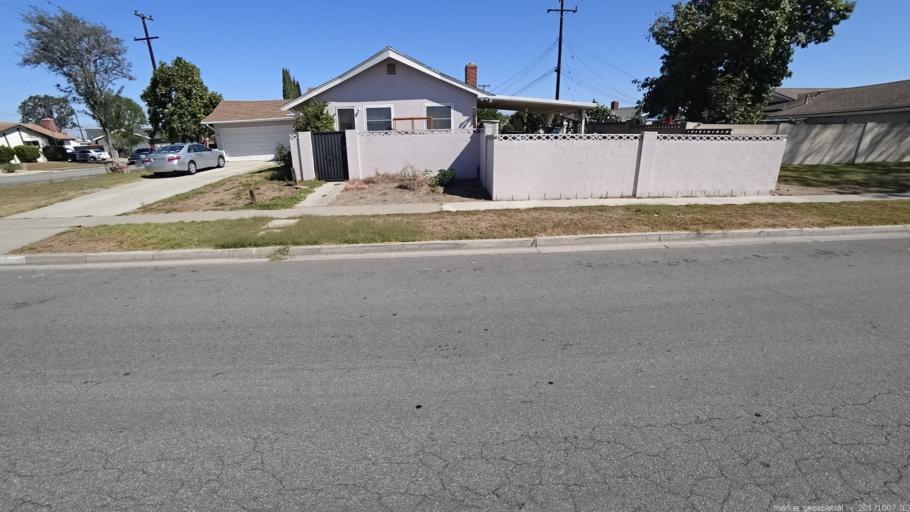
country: US
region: California
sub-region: Orange County
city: Stanton
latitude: 33.7866
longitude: -117.9983
